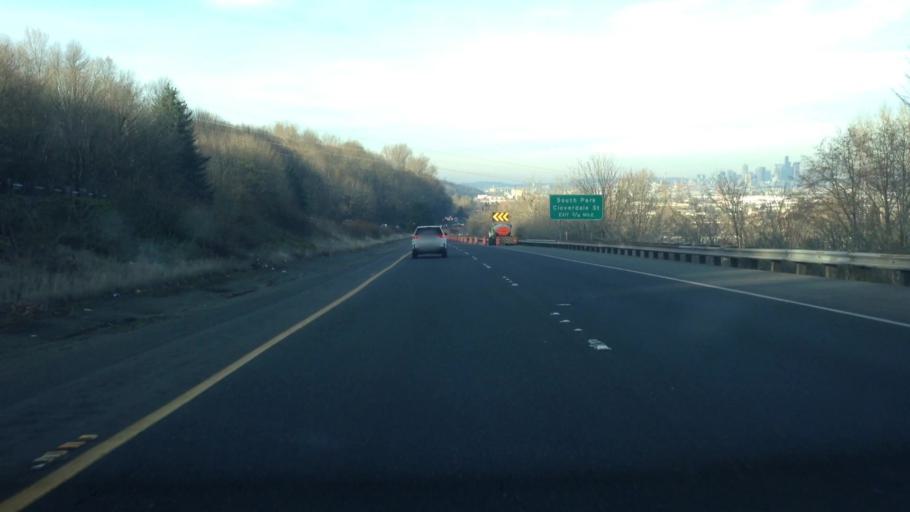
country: US
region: Washington
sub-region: King County
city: White Center
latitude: 47.5139
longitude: -122.3282
